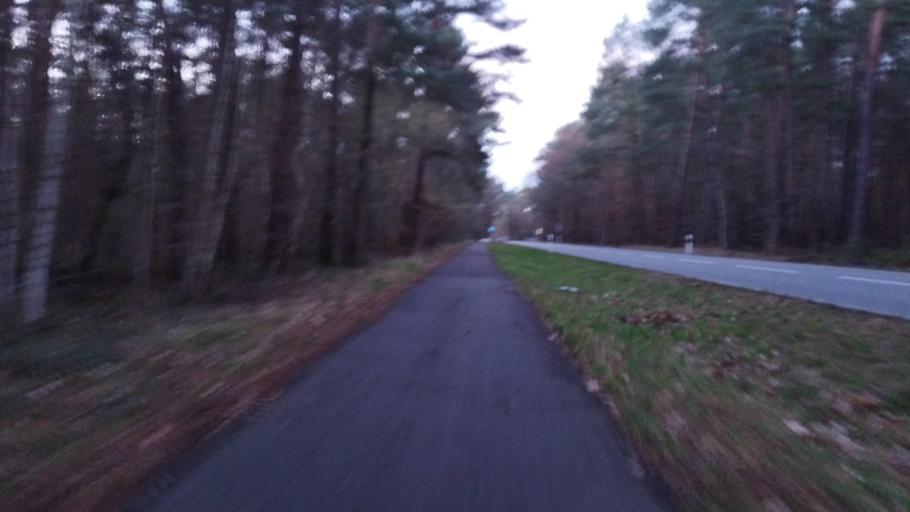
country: DE
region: Rheinland-Pfalz
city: Dudenhofen
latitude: 49.3326
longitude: 8.3749
